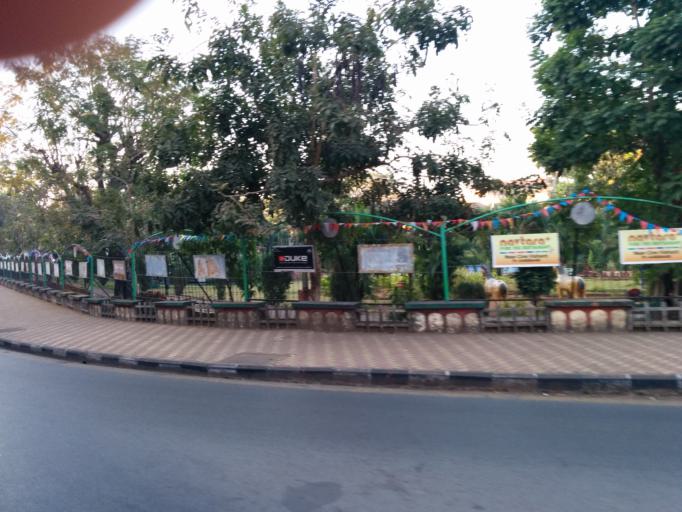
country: IN
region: Goa
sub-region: South Goa
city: Madgaon
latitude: 15.2747
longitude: 73.9582
